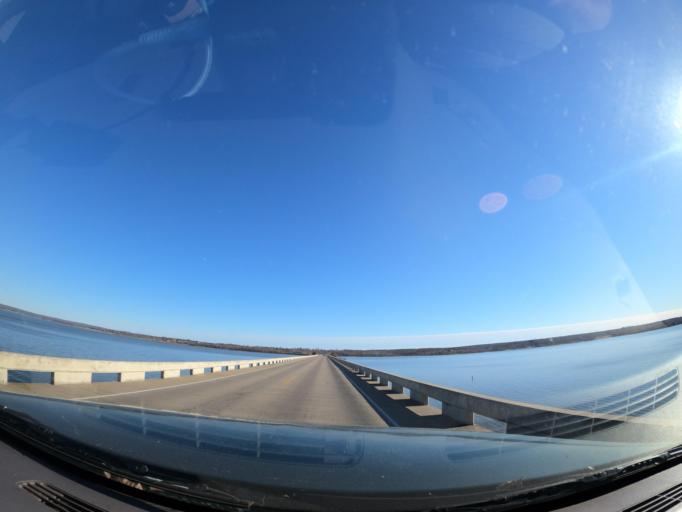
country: US
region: Oklahoma
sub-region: McIntosh County
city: Eufaula
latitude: 35.2464
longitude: -95.5656
